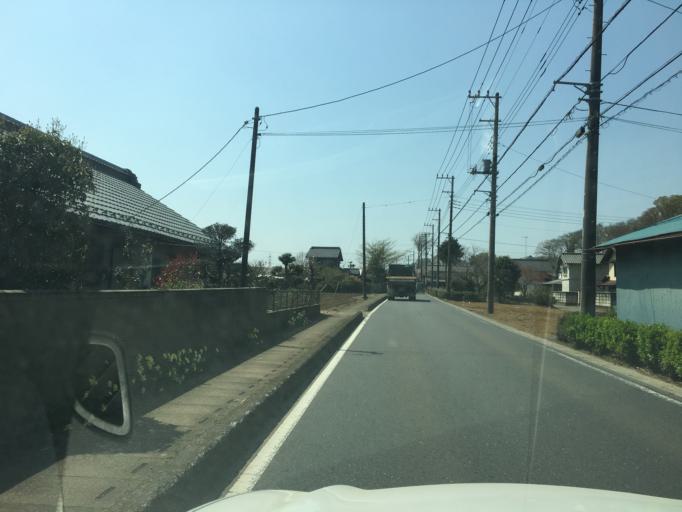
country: JP
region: Saitama
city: Sayama
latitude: 35.8519
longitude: 139.4536
